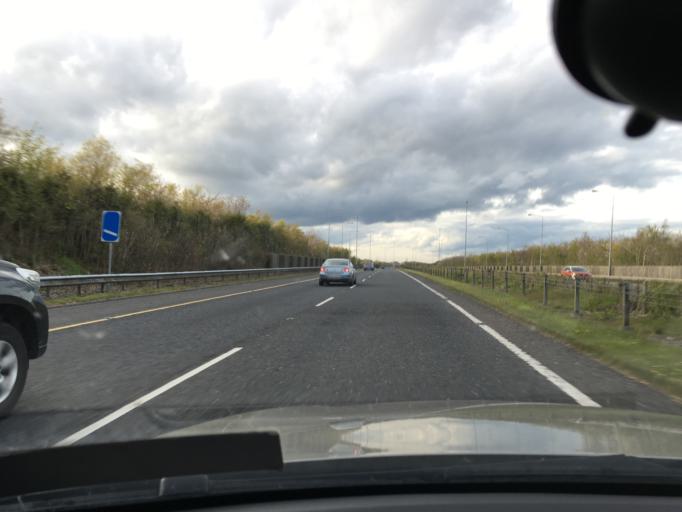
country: IE
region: Leinster
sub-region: Lu
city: Dromiskin
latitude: 53.9621
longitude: -6.4206
